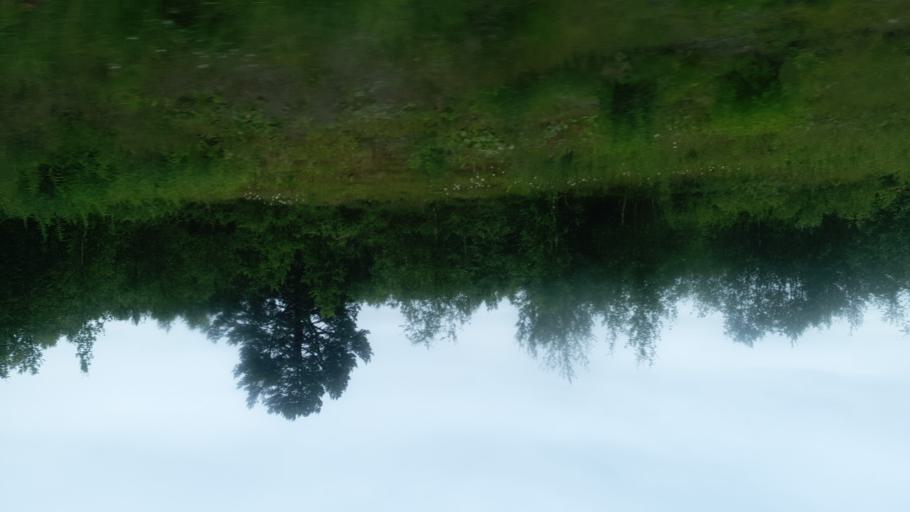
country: NO
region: Oppland
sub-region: Vestre Slidre
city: Slidre
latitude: 61.2383
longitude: 8.9155
